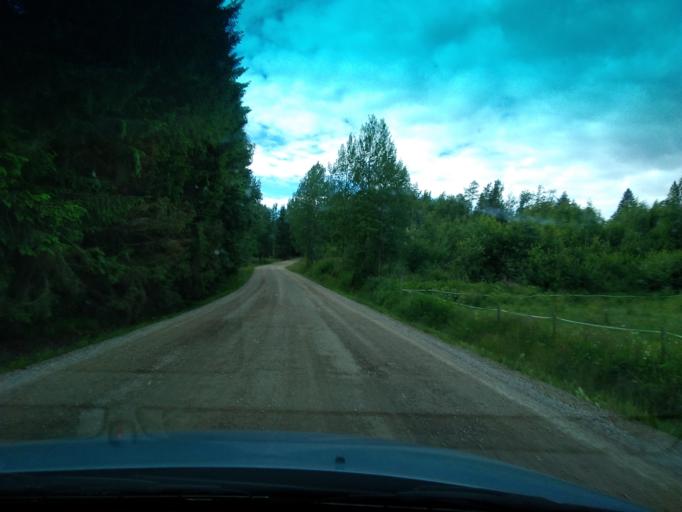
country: FI
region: Central Finland
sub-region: Saarijaervi-Viitasaari
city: Karstula
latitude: 62.8095
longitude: 25.0194
